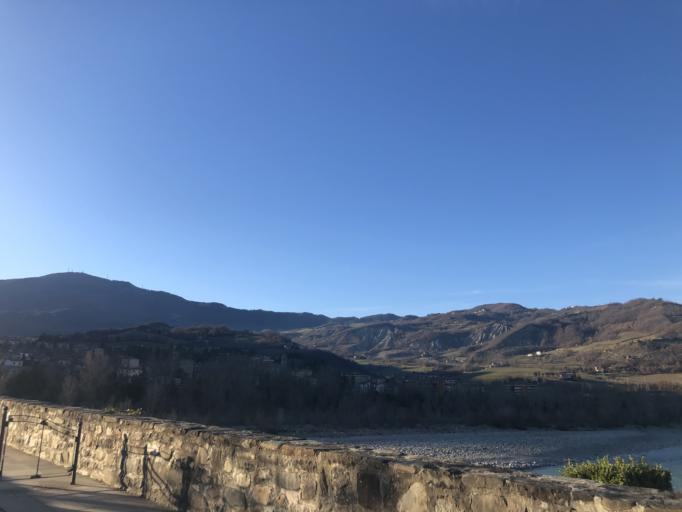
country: IT
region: Emilia-Romagna
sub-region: Provincia di Piacenza
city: Bobbio
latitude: 44.7671
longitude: 9.3927
